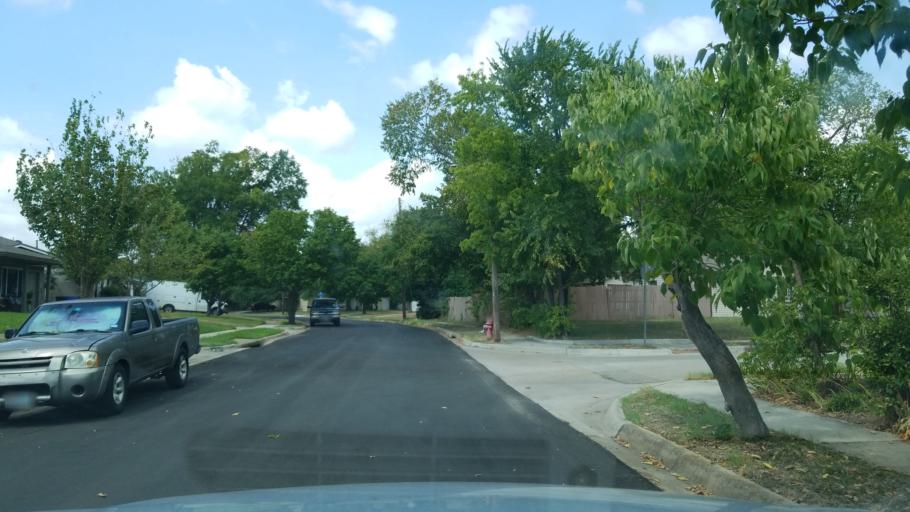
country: US
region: Texas
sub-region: Tarrant County
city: Euless
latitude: 32.8492
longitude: -97.0865
